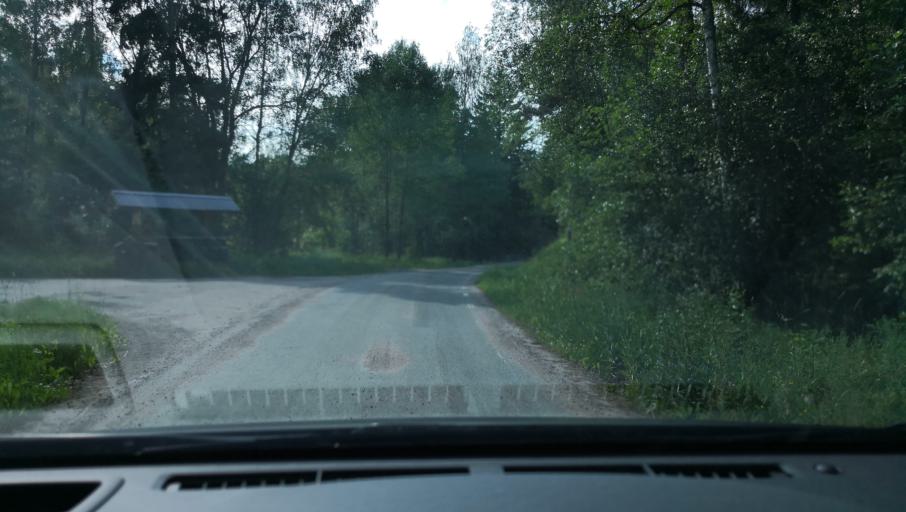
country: SE
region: Uppsala
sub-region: Enkopings Kommun
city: Orsundsbro
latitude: 59.8396
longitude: 17.2053
